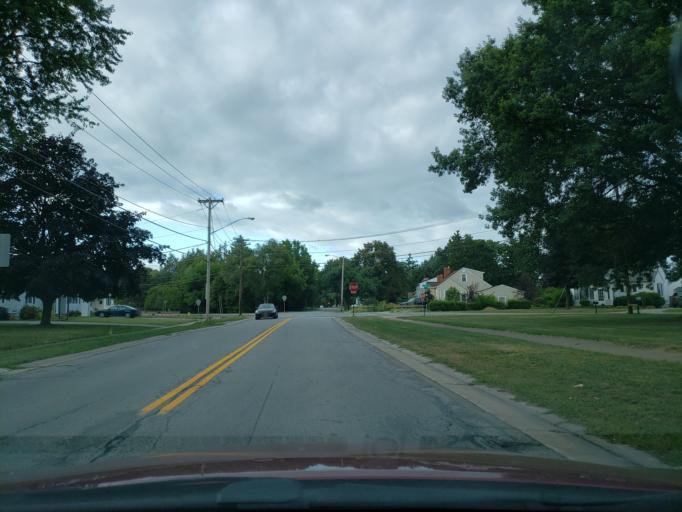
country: US
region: New York
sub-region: Monroe County
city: Greece
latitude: 43.2146
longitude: -77.6516
